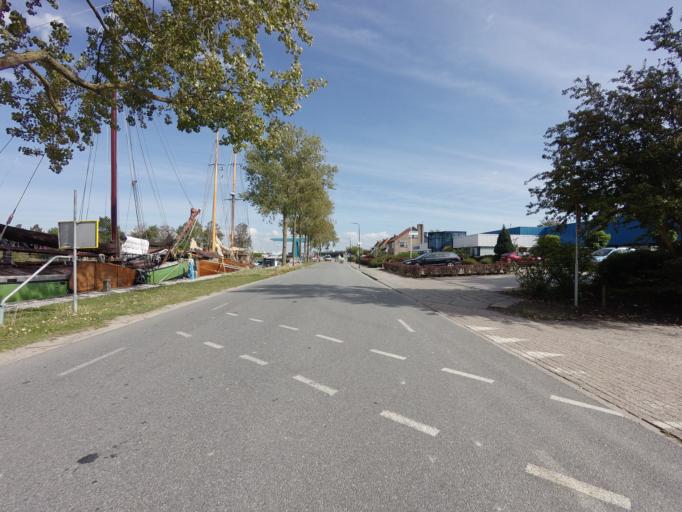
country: NL
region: Friesland
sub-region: Gemeente Harlingen
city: Harlingen
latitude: 53.1744
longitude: 5.4346
